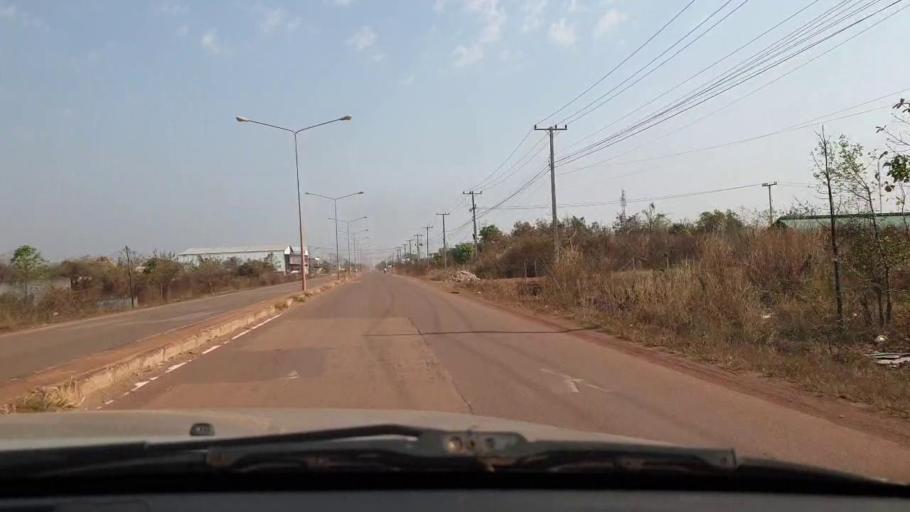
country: LA
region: Vientiane
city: Vientiane
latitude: 18.0063
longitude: 102.7203
